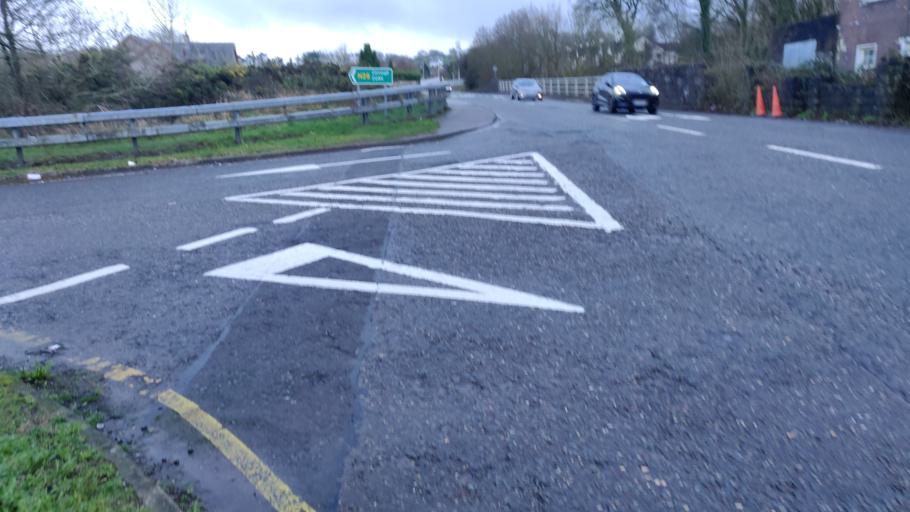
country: IE
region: Munster
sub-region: County Cork
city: Carrigaline
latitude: 51.8669
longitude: -8.4159
